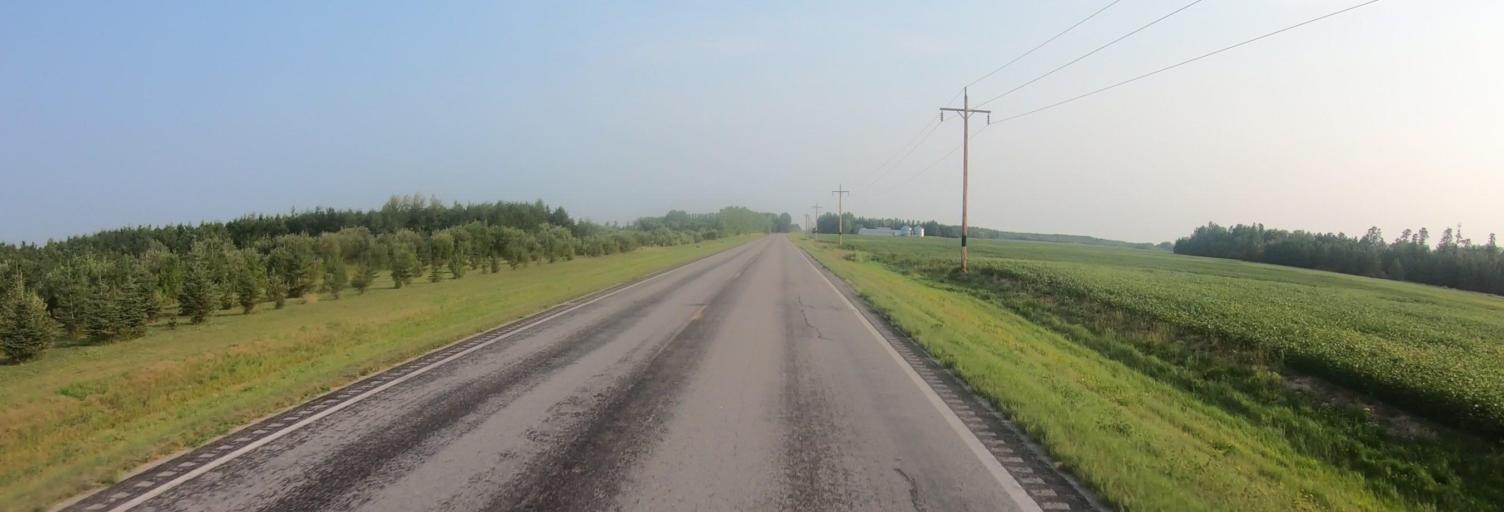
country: US
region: Minnesota
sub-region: Roseau County
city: Warroad
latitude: 48.7888
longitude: -95.3306
